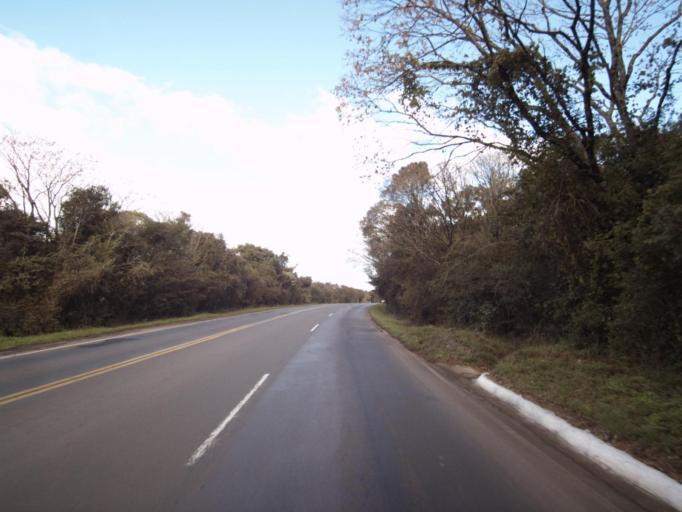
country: BR
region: Santa Catarina
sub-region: Joacaba
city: Joacaba
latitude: -27.2974
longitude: -51.3989
